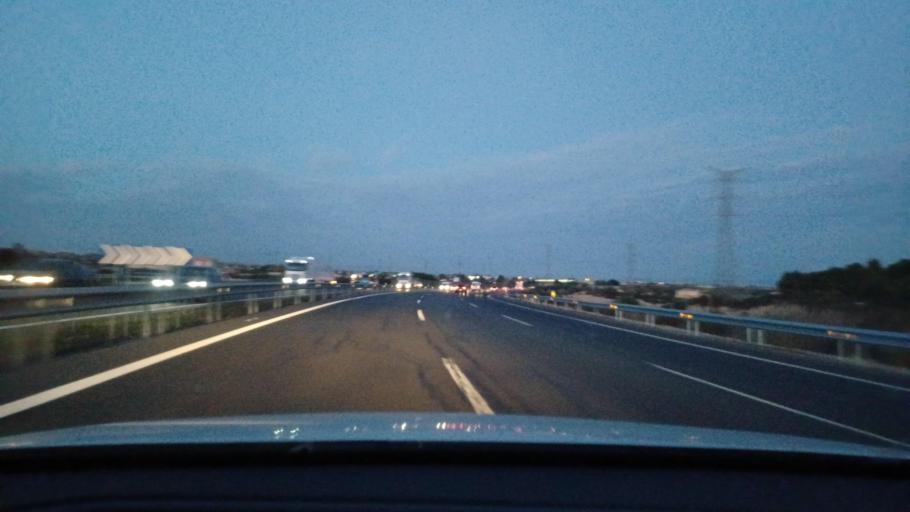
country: ES
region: Valencia
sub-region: Provincia de Alicante
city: Crevillente
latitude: 38.2420
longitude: -0.7799
